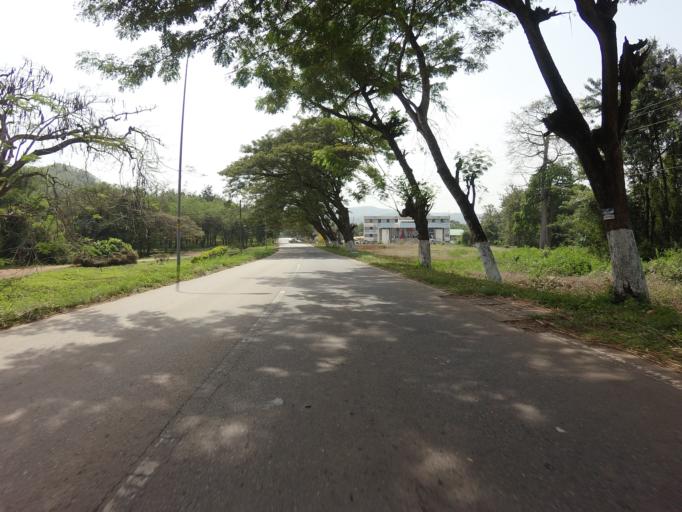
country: GH
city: Akropong
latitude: 6.2764
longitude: 0.0527
